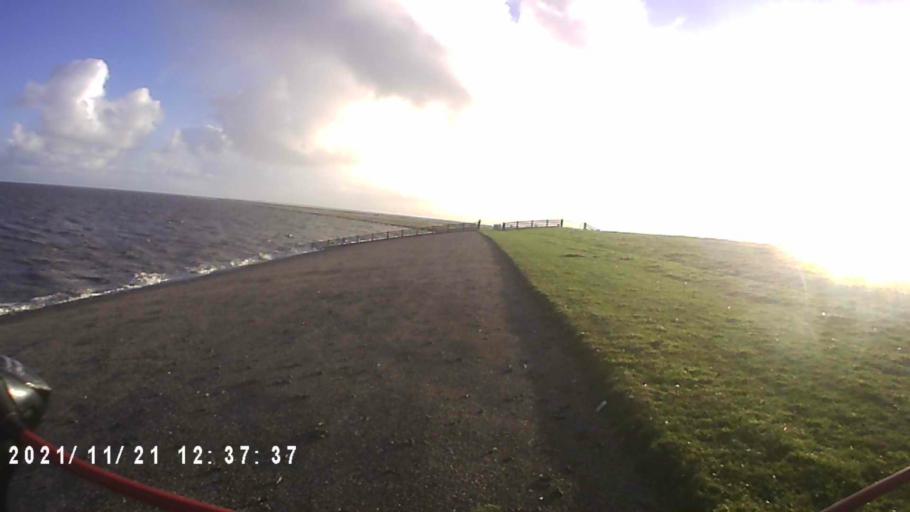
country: NL
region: Friesland
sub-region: Gemeente Dongeradeel
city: Anjum
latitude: 53.4062
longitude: 6.0734
